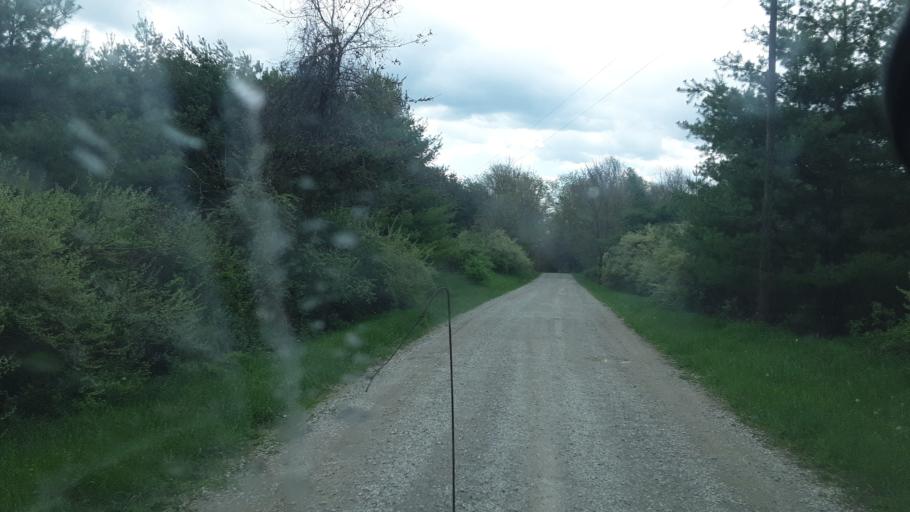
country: US
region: Ohio
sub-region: Noble County
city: Caldwell
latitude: 39.7501
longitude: -81.6190
